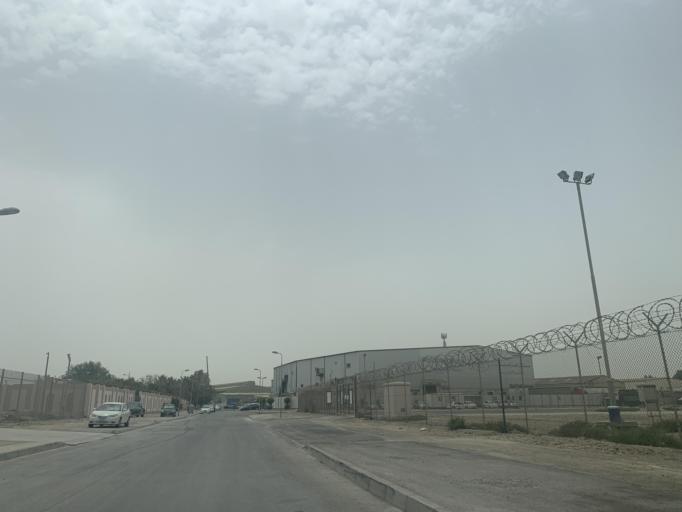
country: BH
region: Northern
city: Sitrah
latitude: 26.1809
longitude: 50.6194
